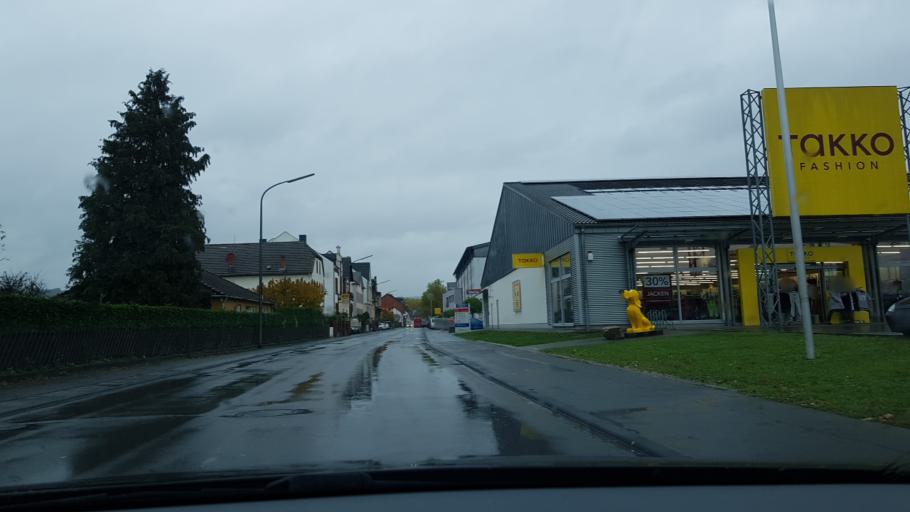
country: DE
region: Rheinland-Pfalz
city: Wittlich
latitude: 49.9818
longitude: 6.8930
